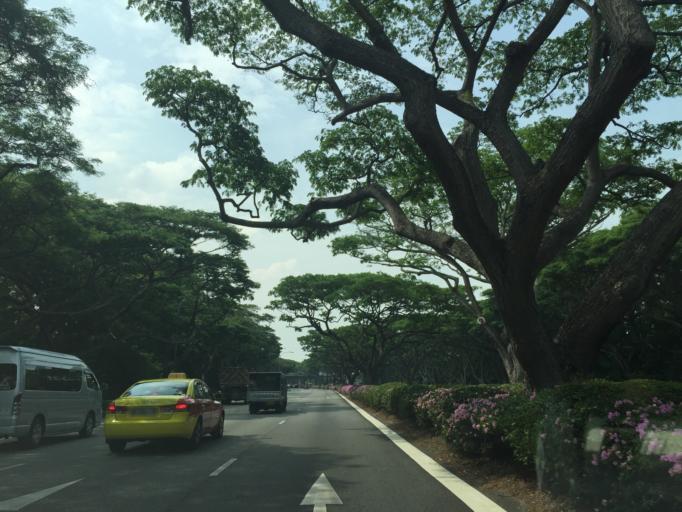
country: SG
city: Singapore
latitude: 1.3342
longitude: 103.9782
